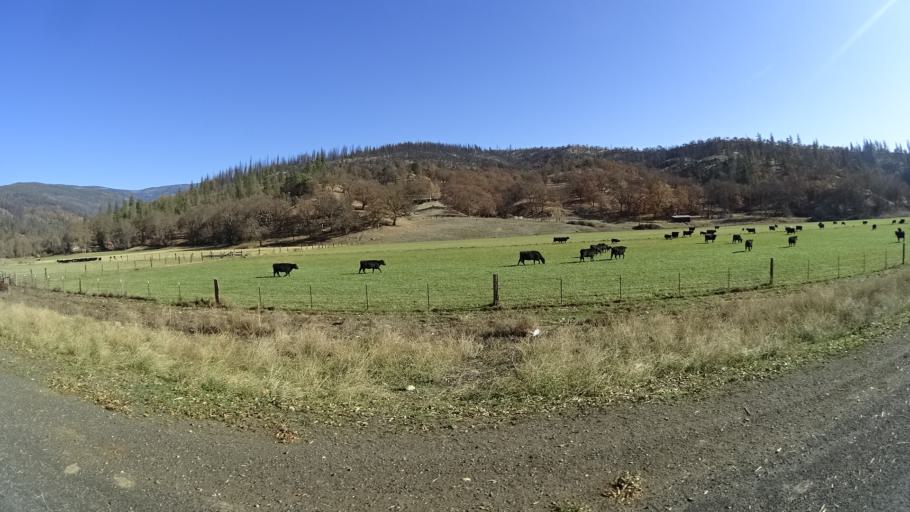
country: US
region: California
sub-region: Siskiyou County
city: Happy Camp
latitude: 41.8319
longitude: -123.0077
